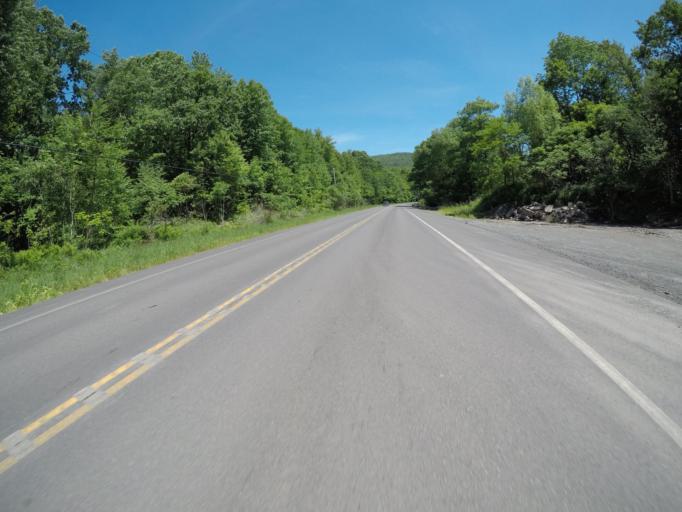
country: US
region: New York
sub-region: Delaware County
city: Walton
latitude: 42.1658
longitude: -75.0429
